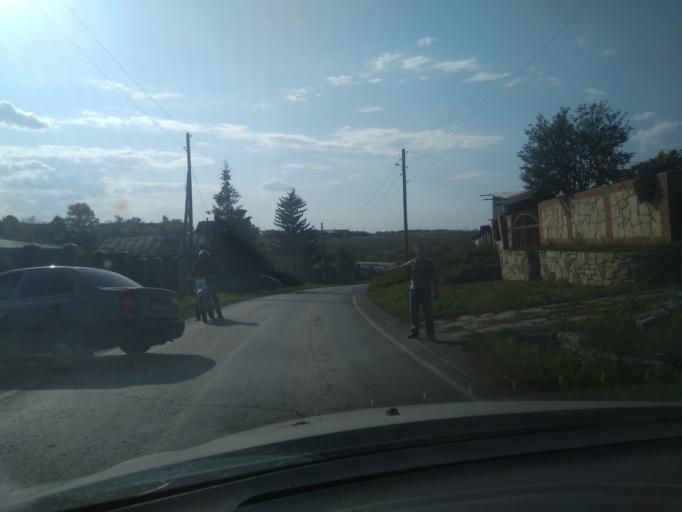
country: RU
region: Sverdlovsk
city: Pokrovskoye
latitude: 56.4365
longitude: 61.5957
